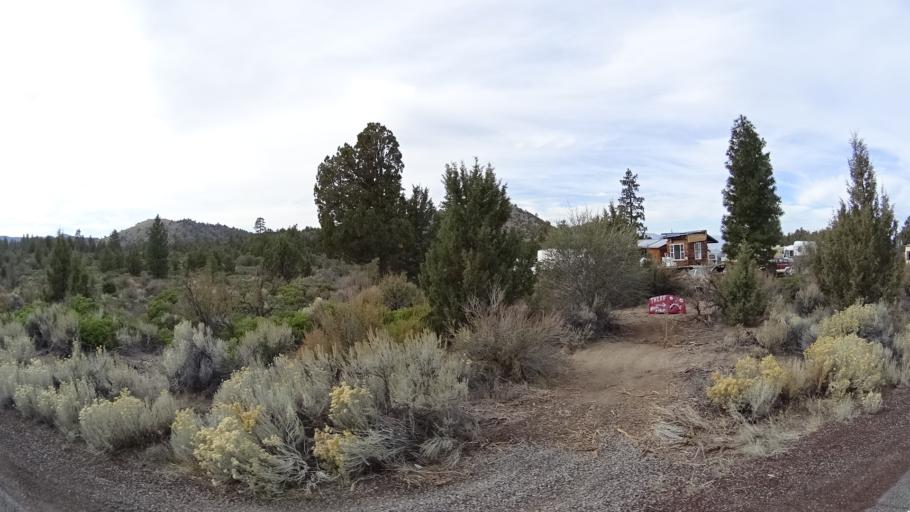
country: US
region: California
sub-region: Siskiyou County
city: Weed
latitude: 41.5492
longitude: -122.2487
